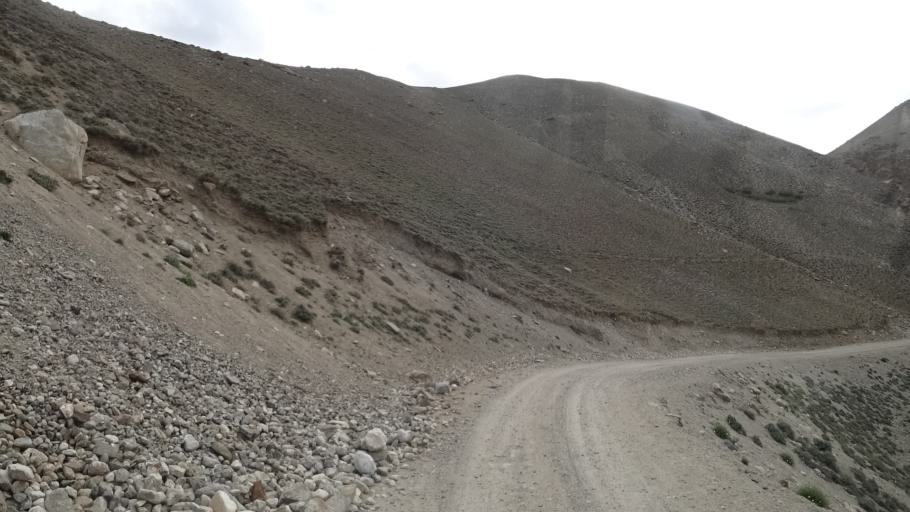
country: AF
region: Badakhshan
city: Khandud
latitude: 37.2186
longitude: 72.7882
